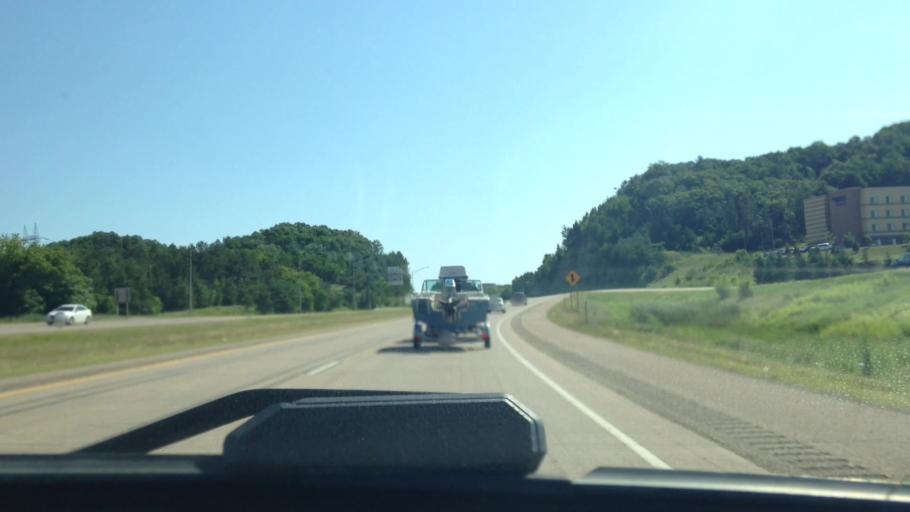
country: US
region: Wisconsin
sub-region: Eau Claire County
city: Seymour
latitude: 44.8357
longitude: -91.4486
